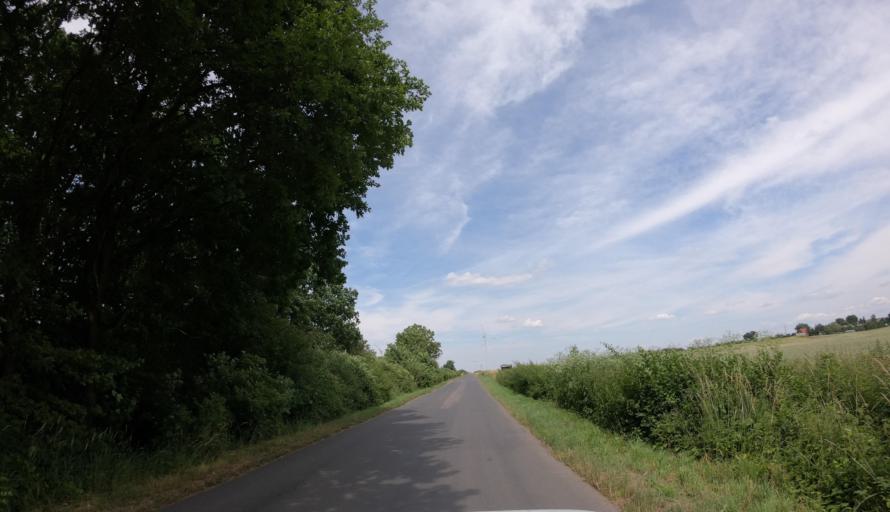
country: PL
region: West Pomeranian Voivodeship
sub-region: Powiat pyrzycki
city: Kozielice
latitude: 53.0810
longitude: 14.8286
